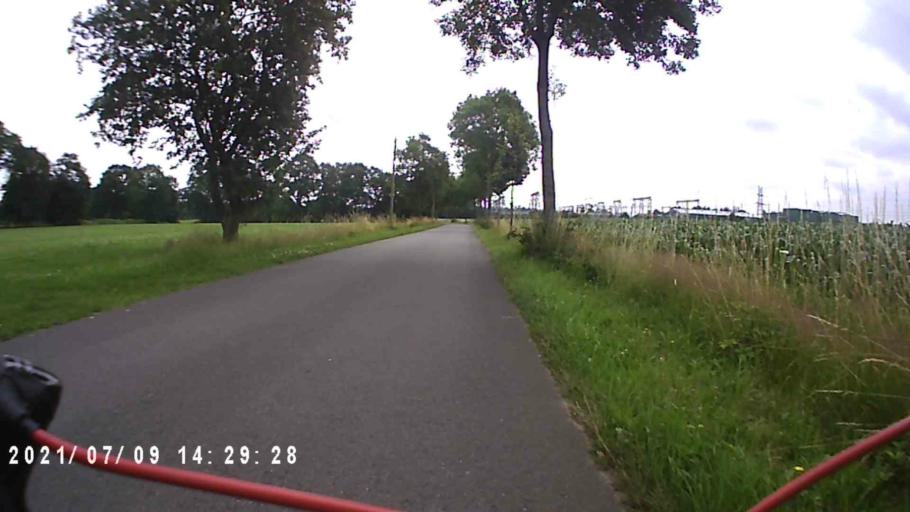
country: DE
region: Lower Saxony
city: Weener
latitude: 53.1279
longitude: 7.3035
